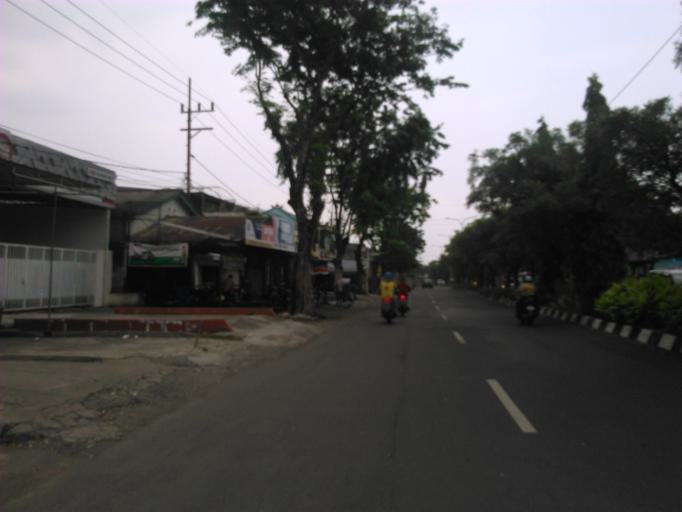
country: ID
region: East Java
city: Gubengairlangga
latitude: -7.2761
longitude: 112.7624
